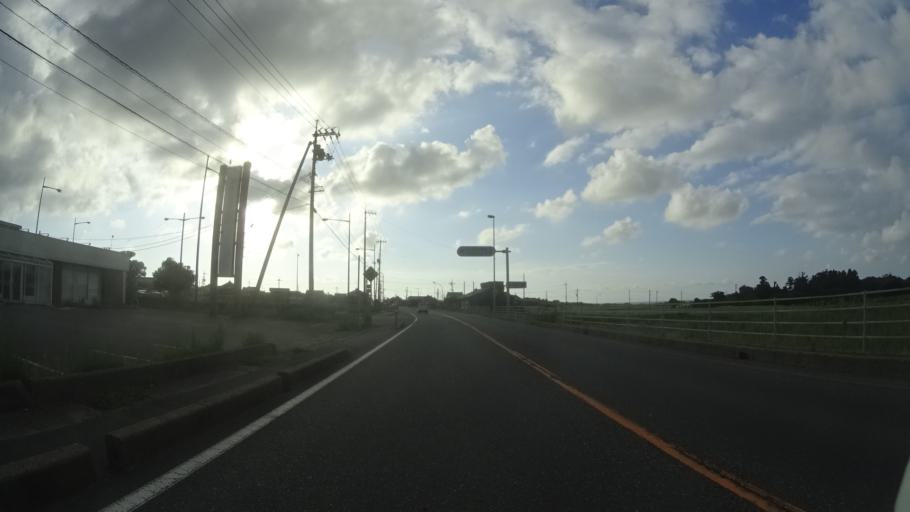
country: JP
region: Tottori
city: Kurayoshi
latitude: 35.5231
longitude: 133.5940
